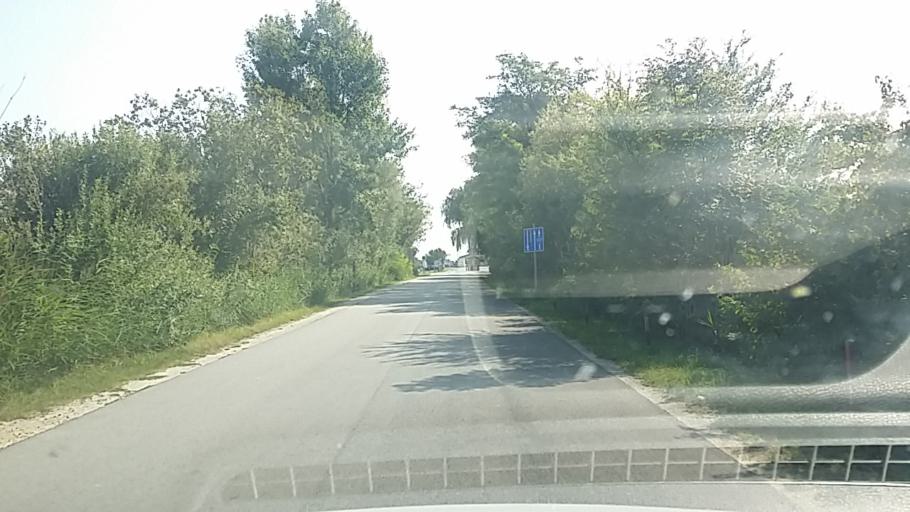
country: AT
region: Burgenland
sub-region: Eisenstadt-Umgebung
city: Morbisch am See
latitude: 47.7199
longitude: 16.6882
